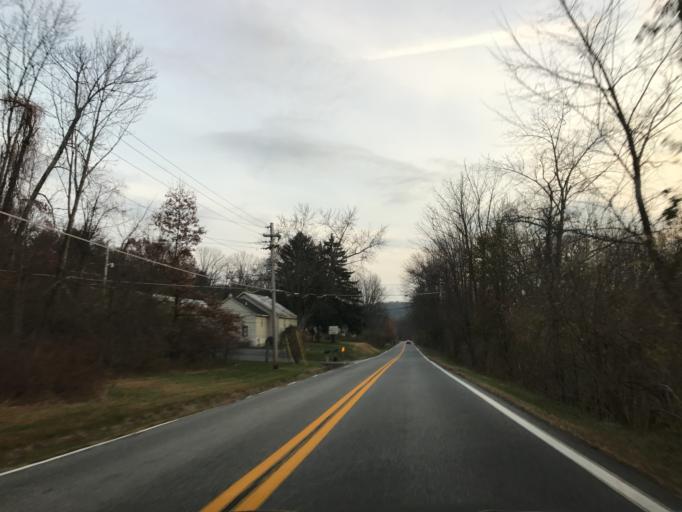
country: US
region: Maryland
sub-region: Frederick County
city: Braddock Heights
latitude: 39.4509
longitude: -77.4954
